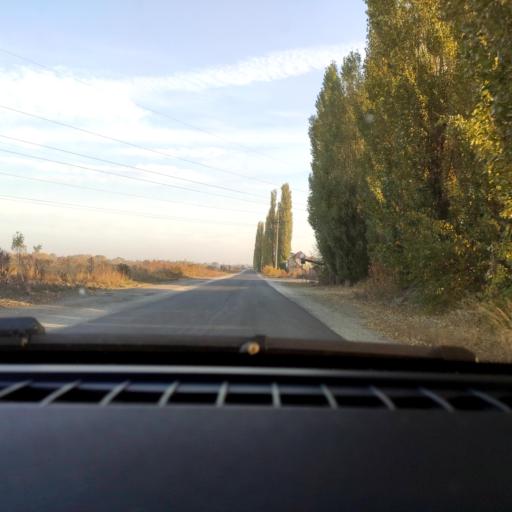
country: RU
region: Voronezj
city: Maslovka
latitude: 51.5229
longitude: 39.2266
